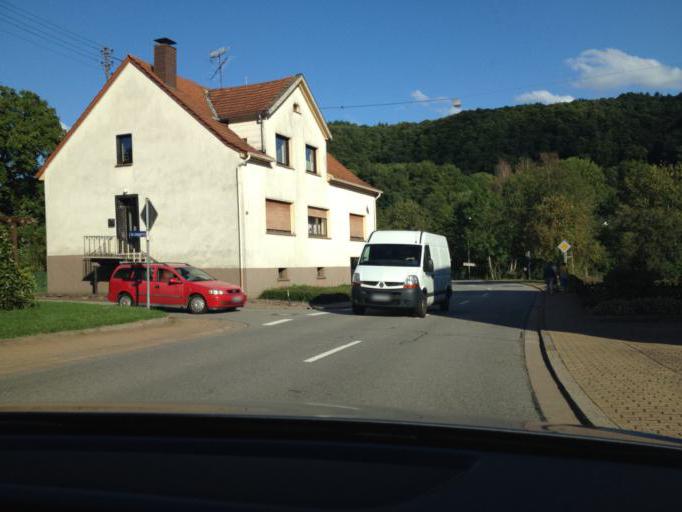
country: DE
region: Saarland
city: Wadern
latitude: 49.4923
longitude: 6.8626
